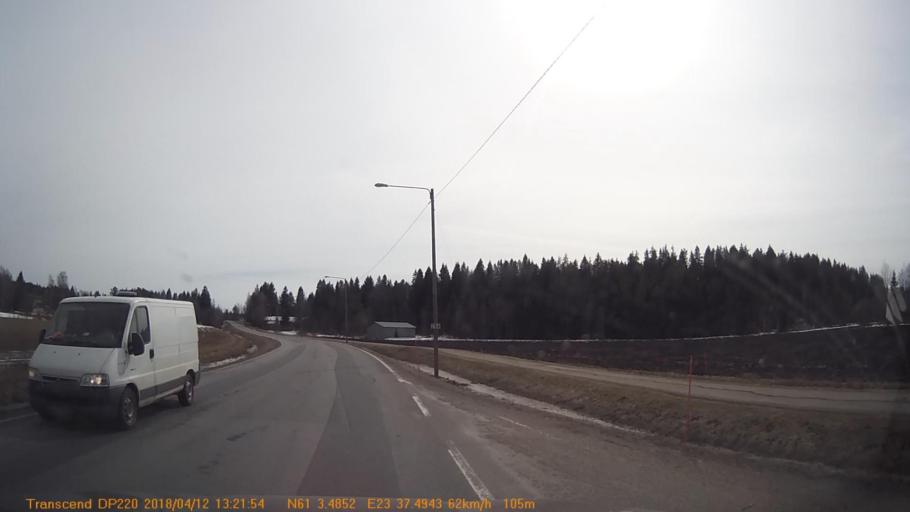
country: FI
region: Pirkanmaa
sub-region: Etelae-Pirkanmaa
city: Urjala
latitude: 61.0569
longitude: 23.6253
